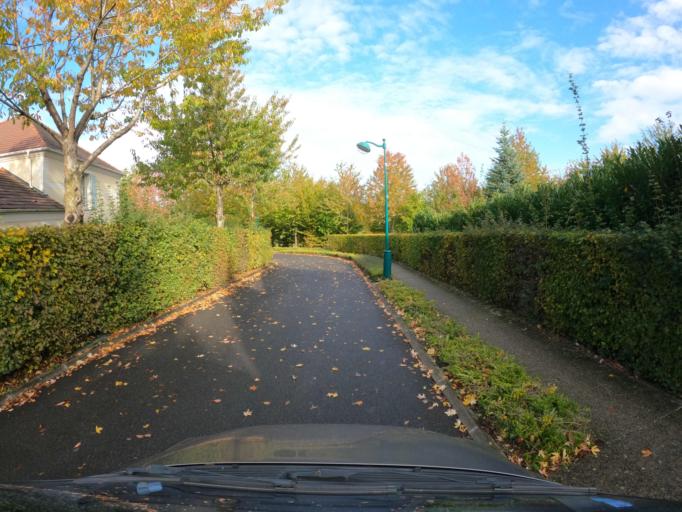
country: FR
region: Ile-de-France
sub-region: Departement de Seine-et-Marne
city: Magny-le-Hongre
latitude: 48.8701
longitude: 2.8221
